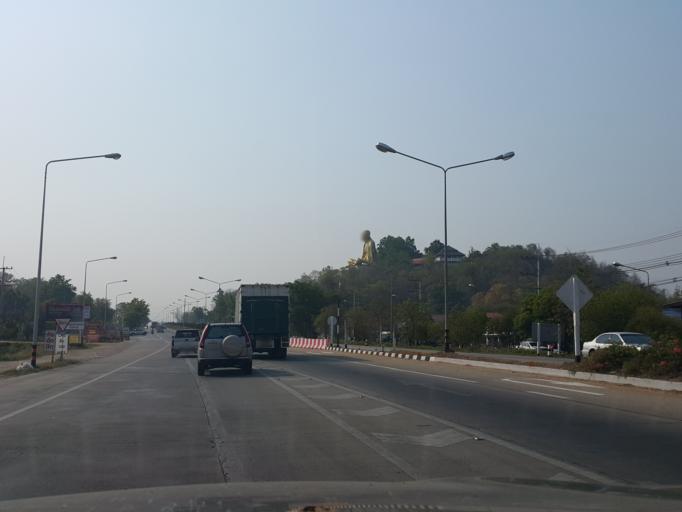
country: TH
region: Lamphun
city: Lamphun
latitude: 18.5508
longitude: 99.0505
